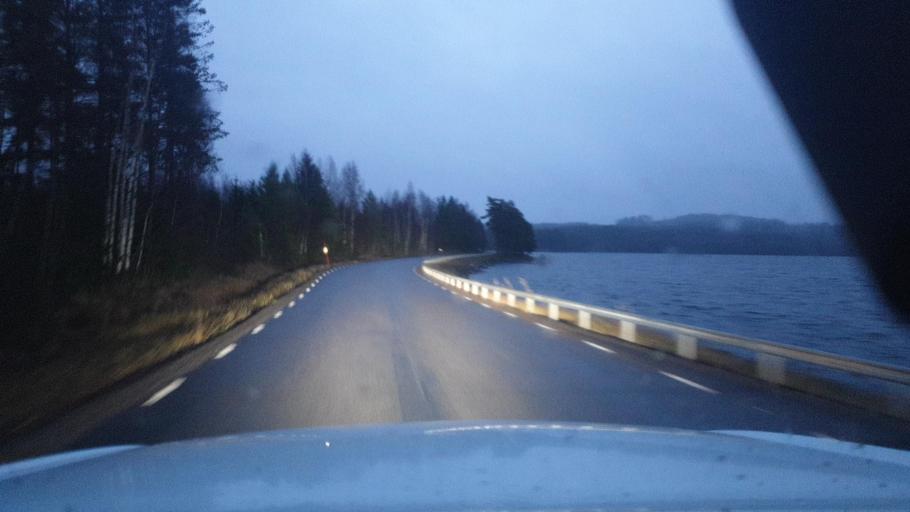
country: SE
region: Vaermland
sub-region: Torsby Kommun
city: Torsby
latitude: 59.9815
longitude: 12.7913
